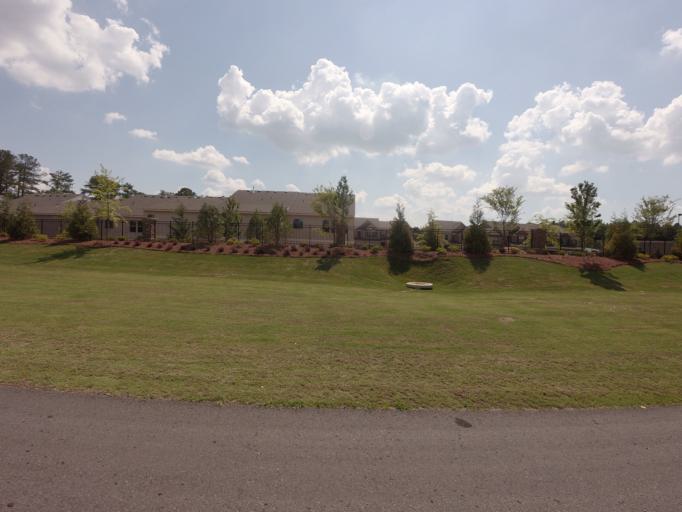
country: US
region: Georgia
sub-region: Fulton County
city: Johns Creek
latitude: 34.0630
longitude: -84.2097
